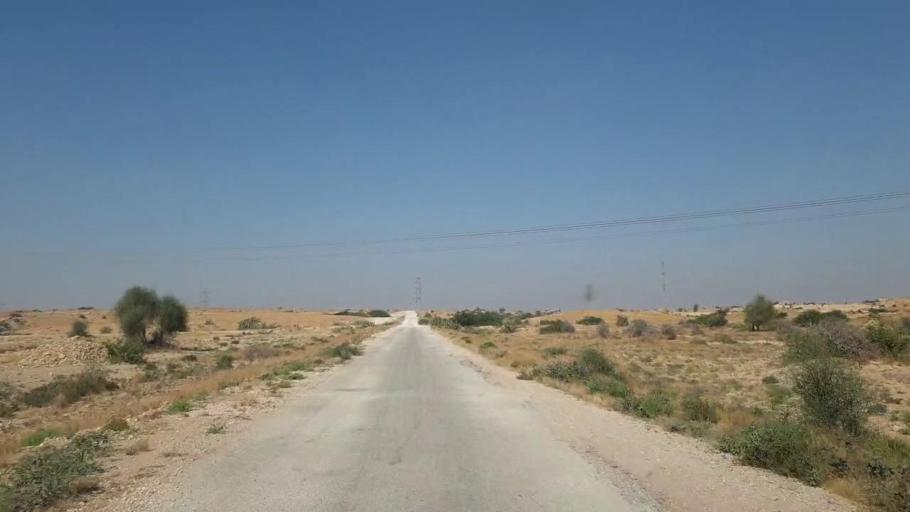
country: PK
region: Sindh
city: Thatta
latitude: 25.1960
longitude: 67.7999
